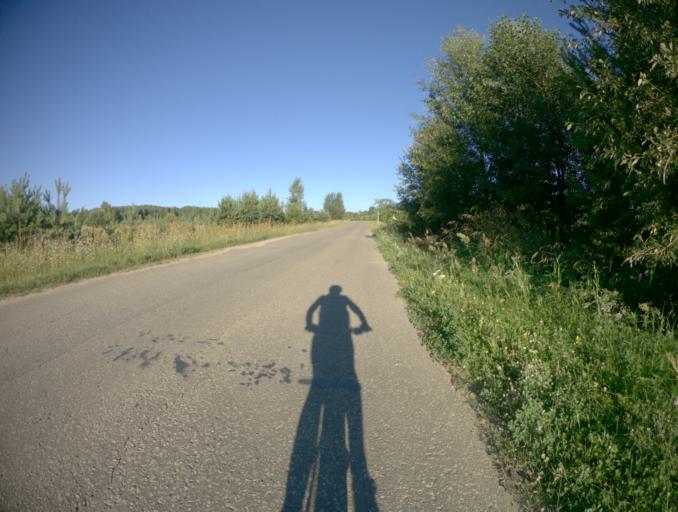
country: RU
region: Vladimir
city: Golovino
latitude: 56.0346
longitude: 40.4377
